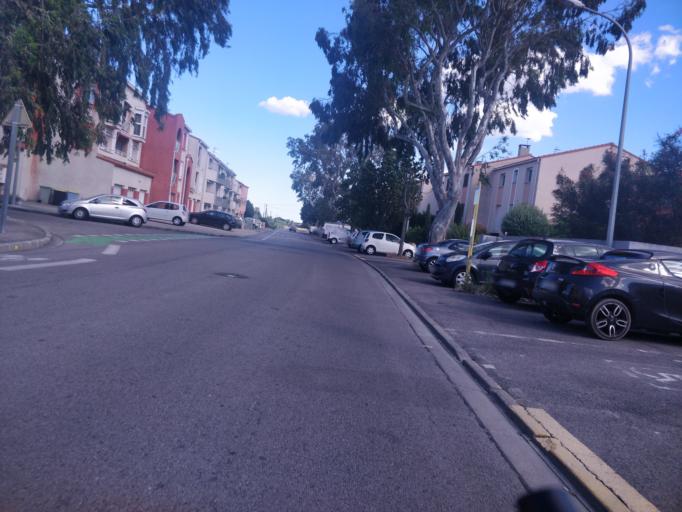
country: FR
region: Languedoc-Roussillon
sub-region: Departement des Pyrenees-Orientales
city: Perpignan
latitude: 42.6832
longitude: 2.9136
